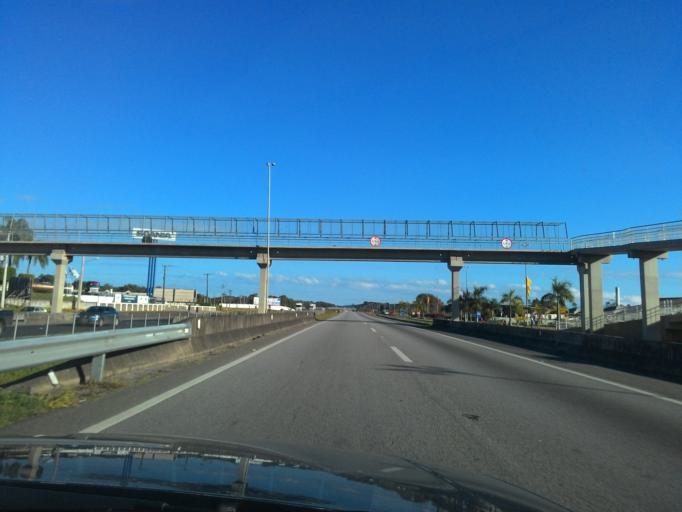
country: BR
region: Sao Paulo
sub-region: Registro
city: Registro
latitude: -24.5296
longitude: -47.8566
